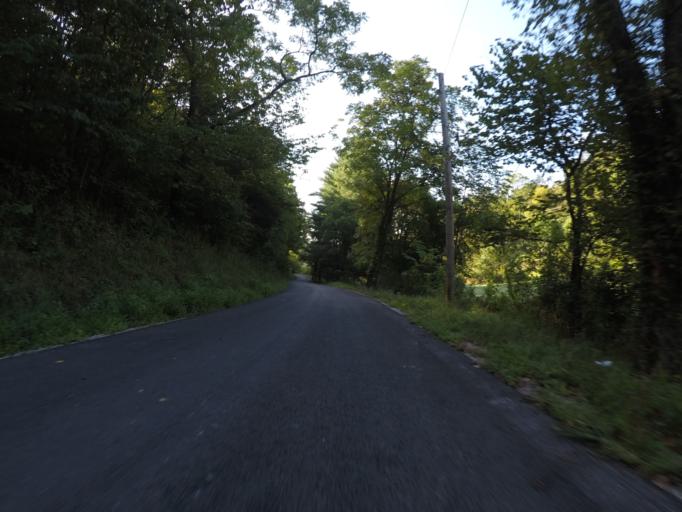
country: US
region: Ohio
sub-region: Lawrence County
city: Burlington
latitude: 38.5172
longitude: -82.5256
